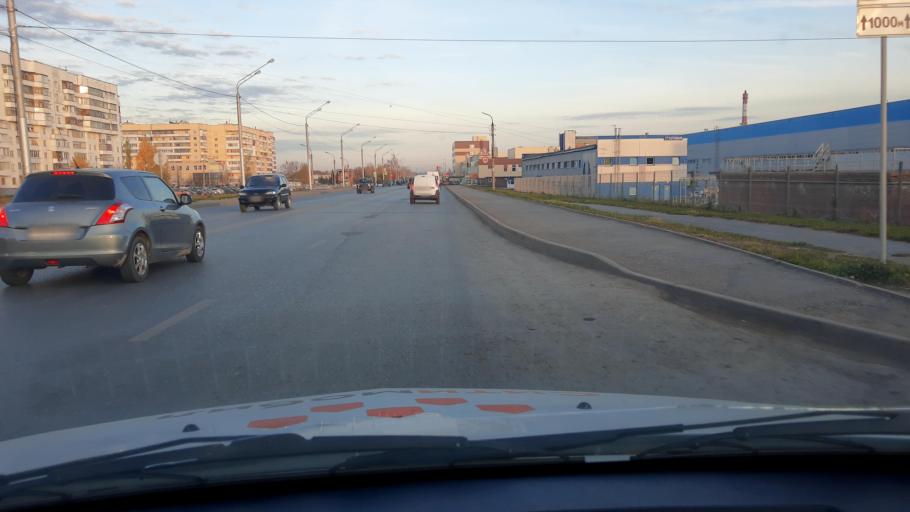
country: RU
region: Bashkortostan
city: Iglino
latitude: 54.7564
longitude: 56.2488
